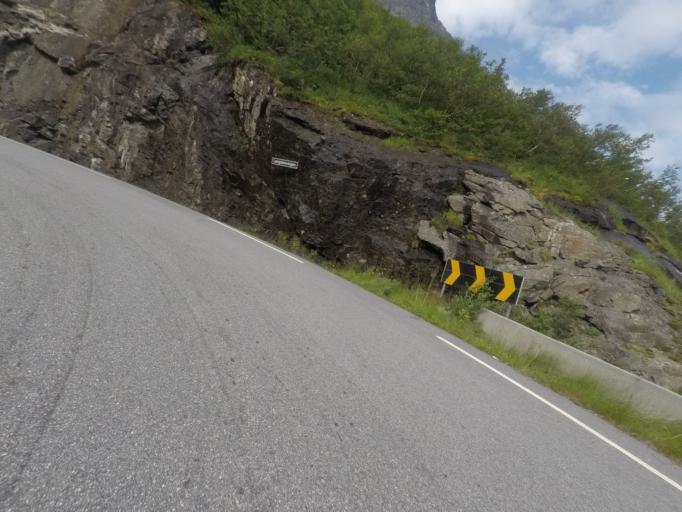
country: NO
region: More og Romsdal
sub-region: Rauma
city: Andalsnes
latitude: 62.4601
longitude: 7.6704
